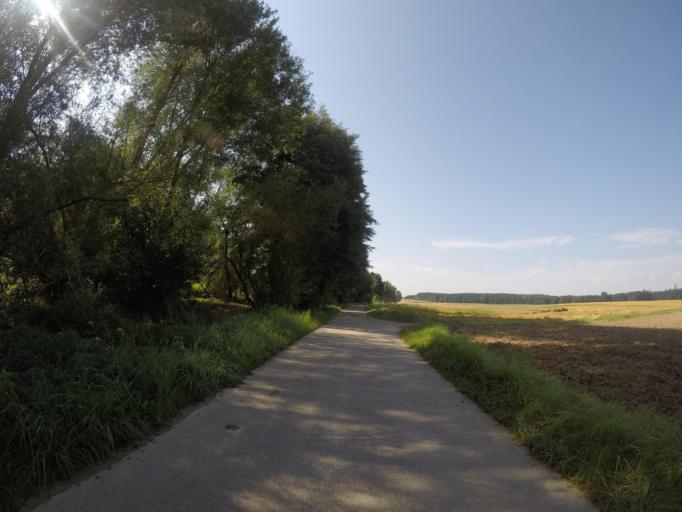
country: DE
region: Baden-Wuerttemberg
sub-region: Tuebingen Region
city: Wain
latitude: 48.2044
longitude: 10.0188
